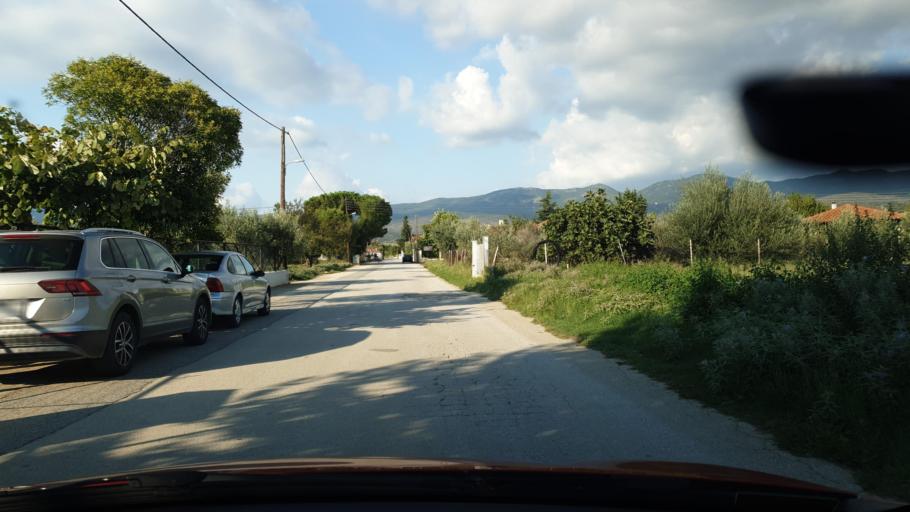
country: GR
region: Central Macedonia
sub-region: Nomos Thessalonikis
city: Vasilika
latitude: 40.4891
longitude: 23.1389
